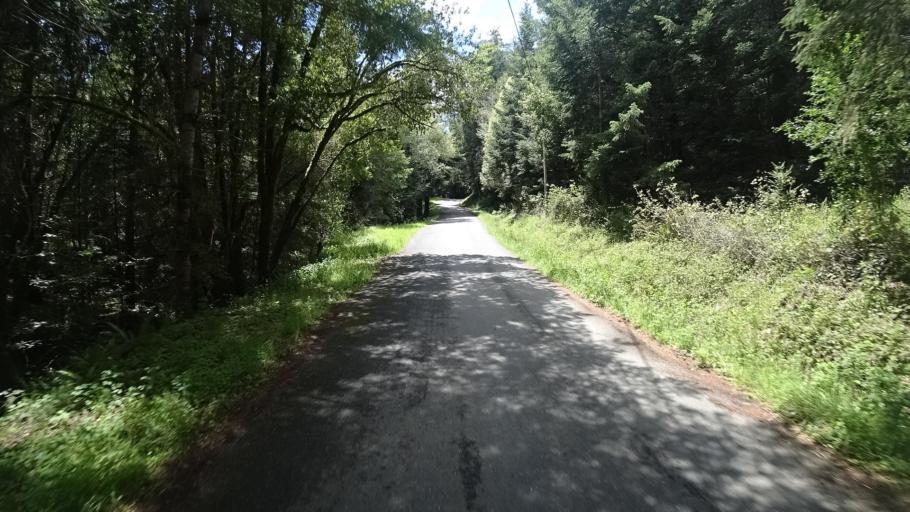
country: US
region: California
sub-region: Humboldt County
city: Blue Lake
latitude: 40.8449
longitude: -123.9145
